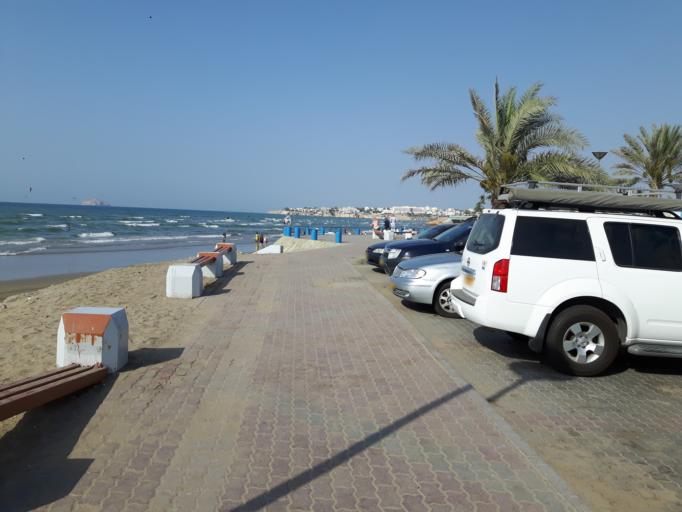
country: OM
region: Muhafazat Masqat
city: Bawshar
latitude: 23.6190
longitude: 58.4675
